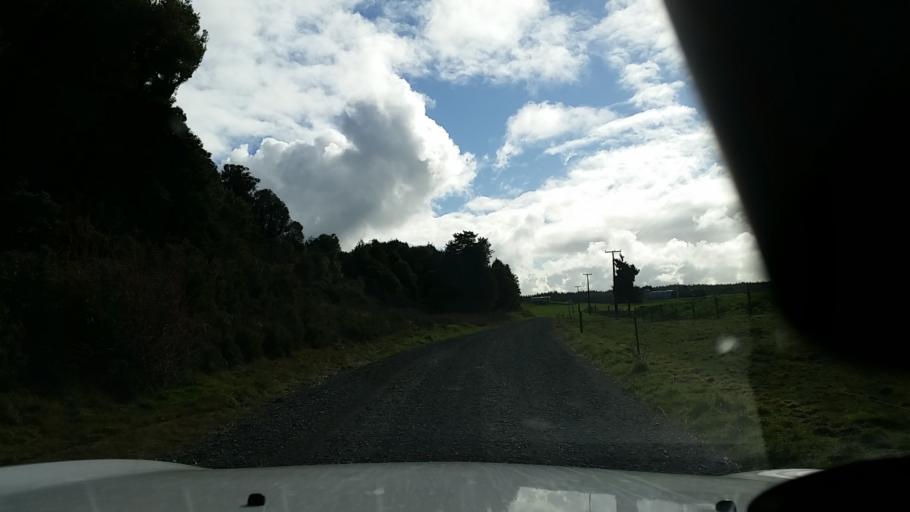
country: NZ
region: Bay of Plenty
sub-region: Rotorua District
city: Rotorua
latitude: -38.0812
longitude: 176.0418
